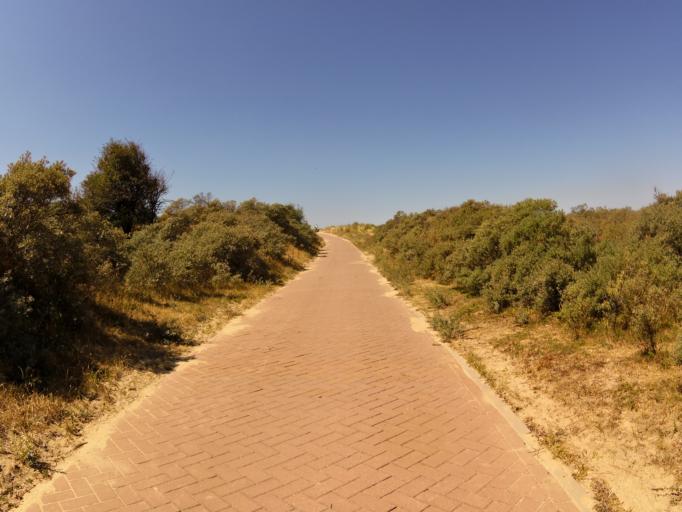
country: NL
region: North Holland
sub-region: Gemeente Zandvoort
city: Zandvoort
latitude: 52.4255
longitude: 4.5645
